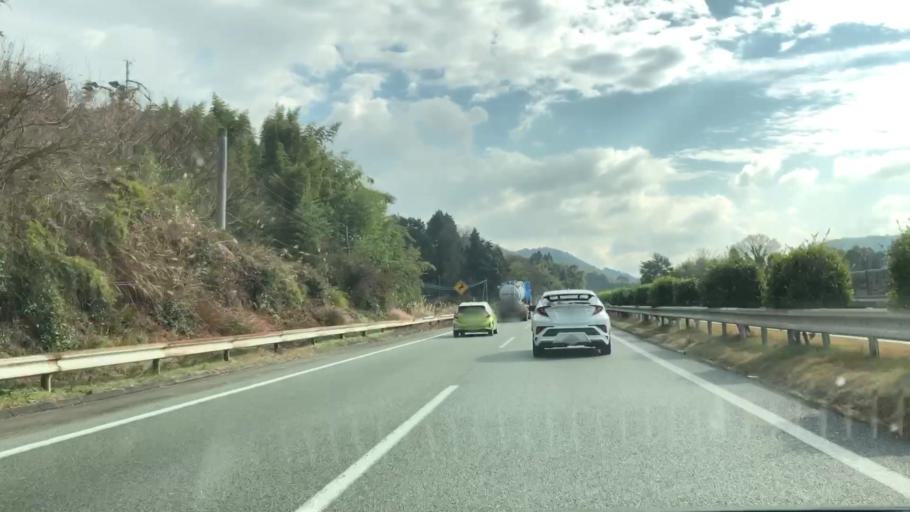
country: JP
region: Fukuoka
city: Setakamachi-takayanagi
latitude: 33.1112
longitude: 130.5316
